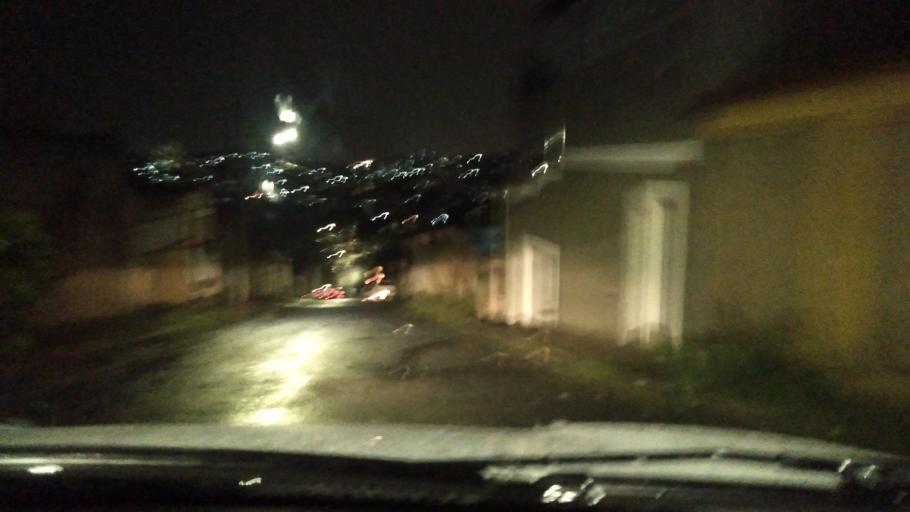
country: BR
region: Minas Gerais
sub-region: Belo Horizonte
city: Belo Horizonte
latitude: -19.9003
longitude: -43.9582
